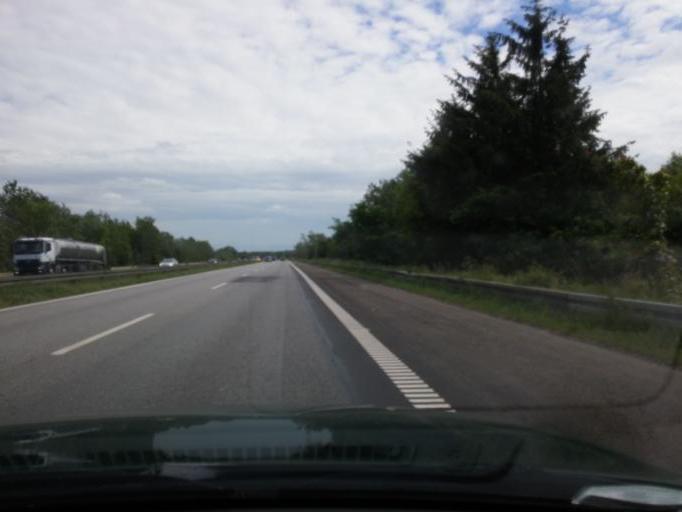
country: DK
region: South Denmark
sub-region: Middelfart Kommune
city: Ejby
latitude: 55.4421
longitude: 9.9691
